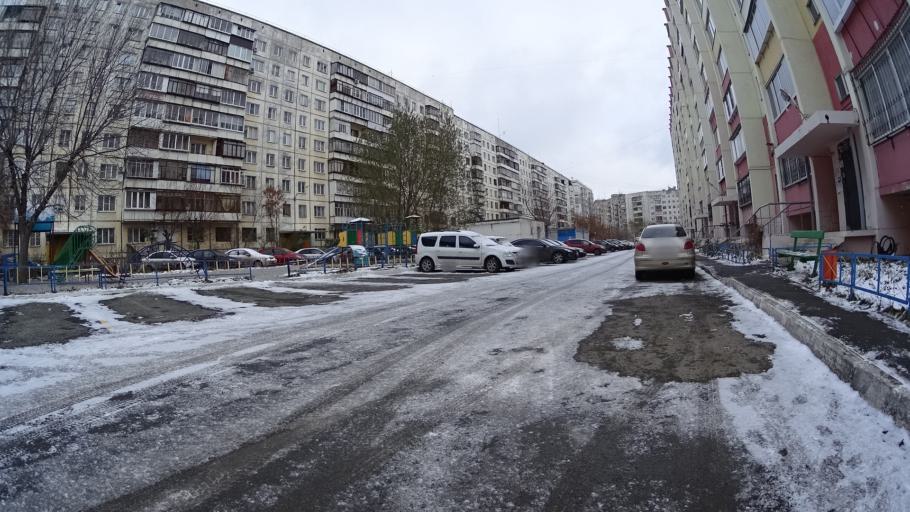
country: RU
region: Chelyabinsk
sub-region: Gorod Chelyabinsk
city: Chelyabinsk
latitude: 55.1880
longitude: 61.3240
